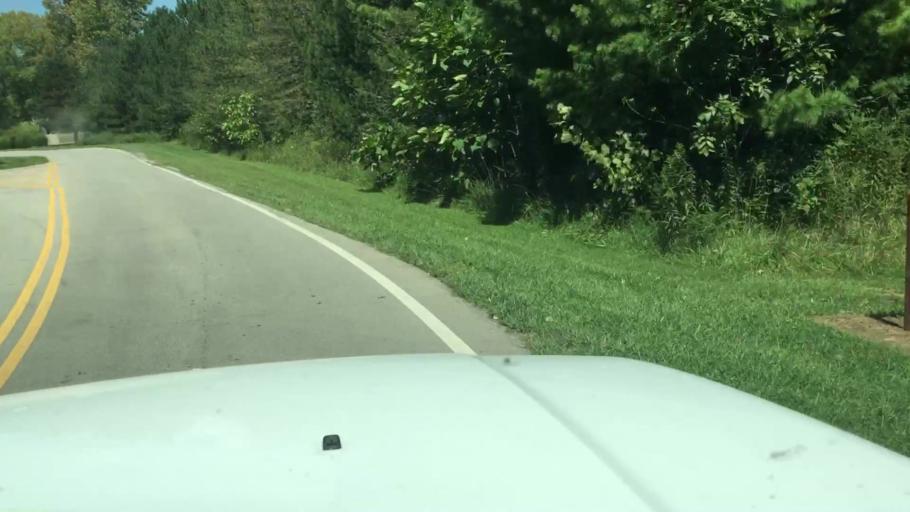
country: US
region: Ohio
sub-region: Madison County
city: Mount Sterling
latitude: 39.6397
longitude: -83.2412
